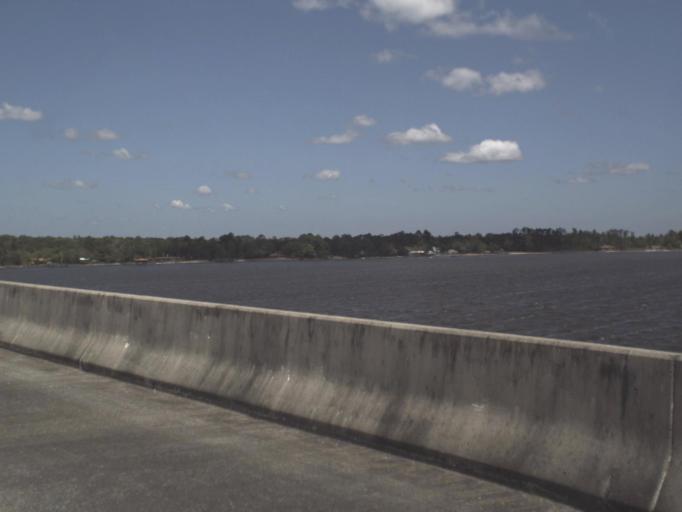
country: US
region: Florida
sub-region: Escambia County
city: Myrtle Grove
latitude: 30.4043
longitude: -87.4296
